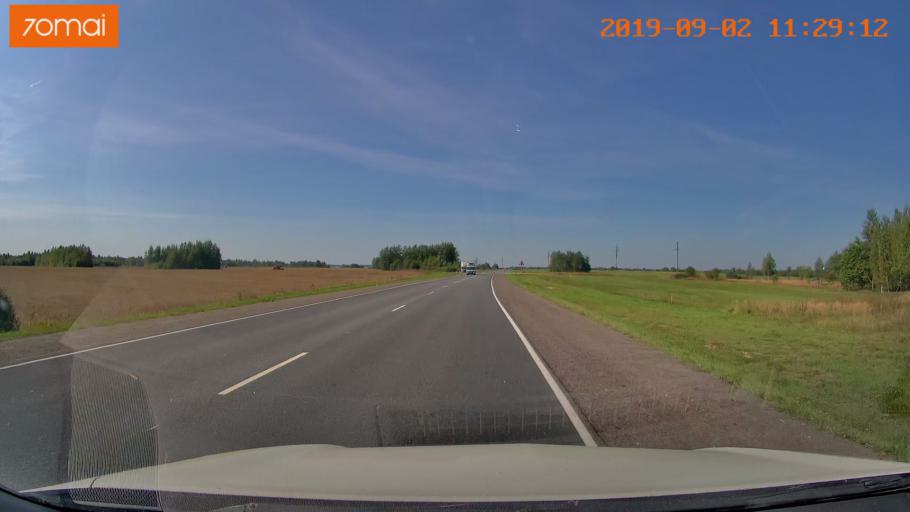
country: RU
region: Smolensk
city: Roslavl'
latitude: 53.9907
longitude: 32.8691
